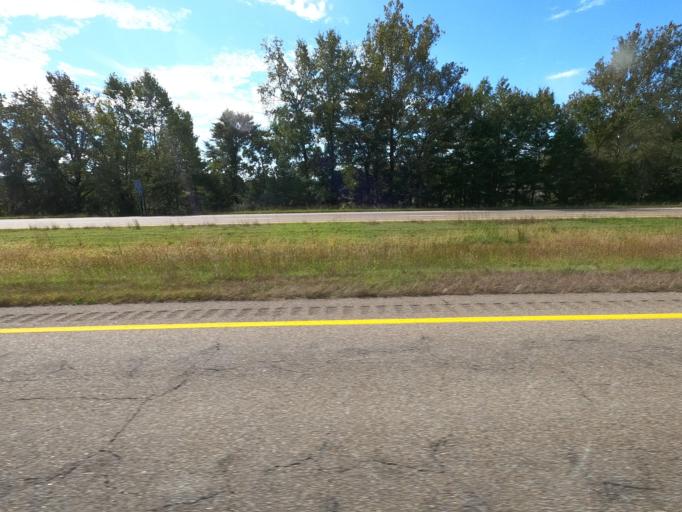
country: US
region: Tennessee
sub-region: Lauderdale County
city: Halls
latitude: 35.8947
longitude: -89.2405
